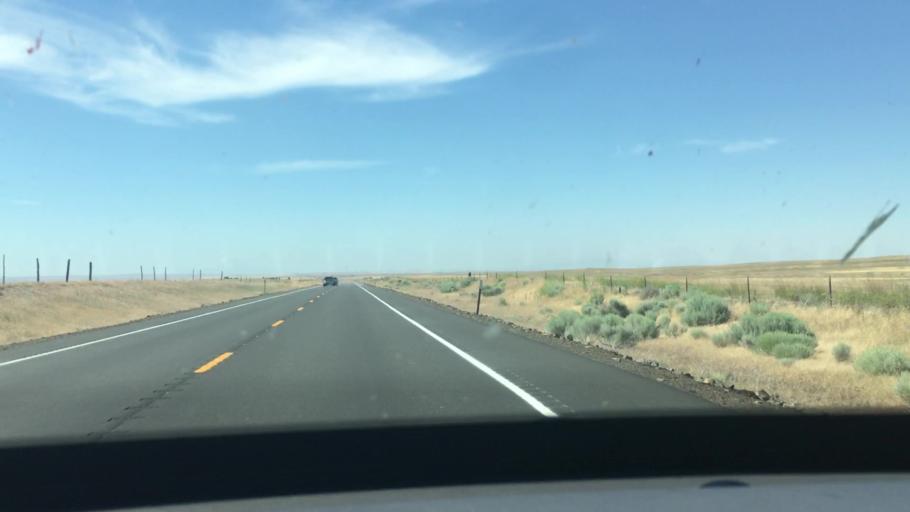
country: US
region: Oregon
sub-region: Sherman County
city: Moro
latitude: 45.2014
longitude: -120.6981
